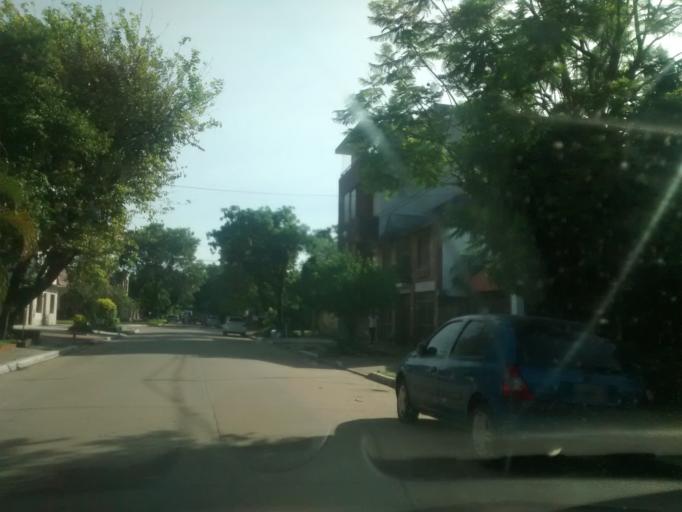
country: AR
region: Chaco
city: Resistencia
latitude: -27.4524
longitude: -58.9774
